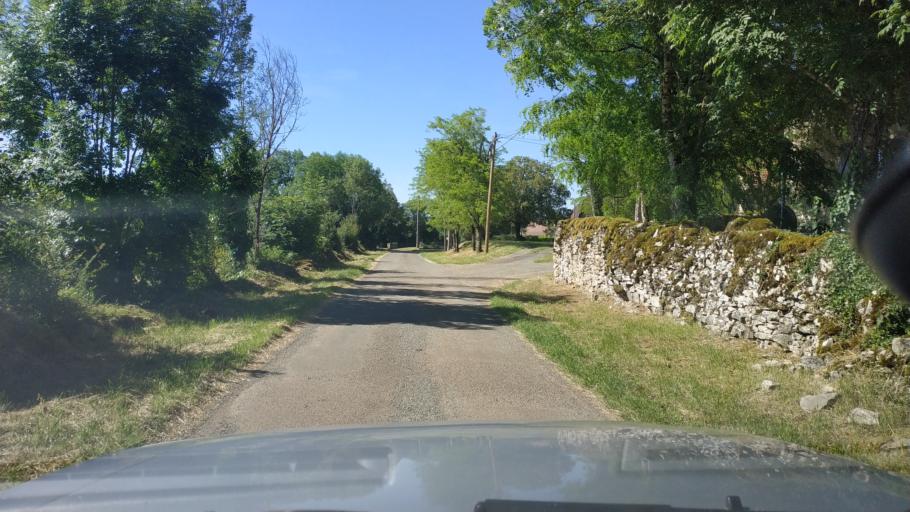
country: FR
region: Midi-Pyrenees
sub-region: Departement du Lot
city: Lacapelle-Marival
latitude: 44.6292
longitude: 1.8706
